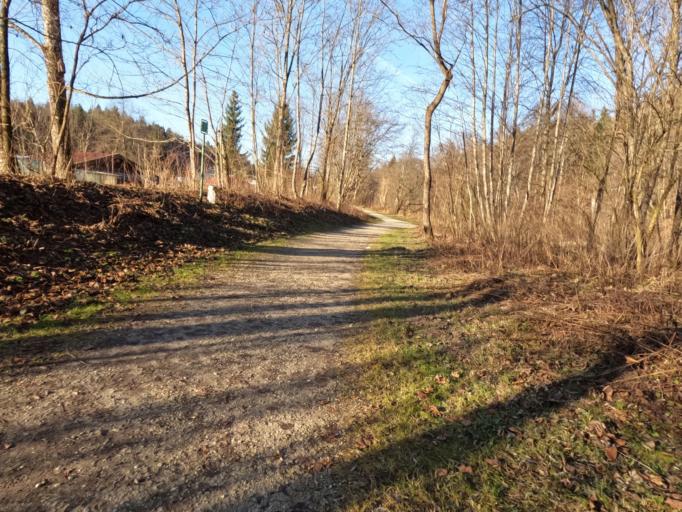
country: DE
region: Bavaria
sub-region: Upper Bavaria
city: Traunstein
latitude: 47.8842
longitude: 12.6421
